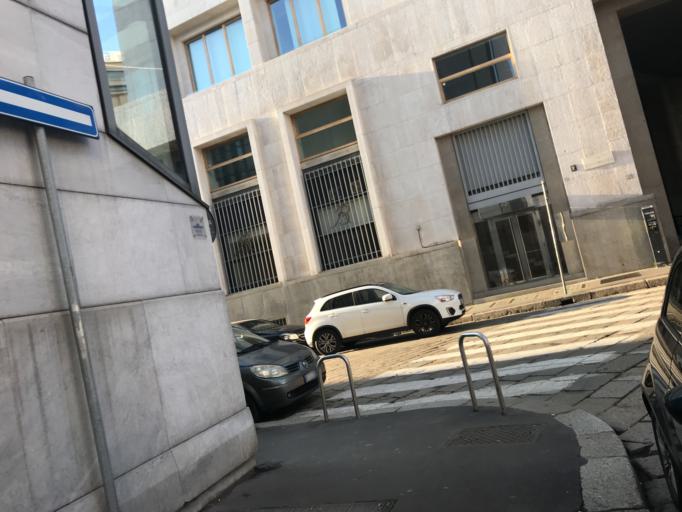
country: IT
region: Lombardy
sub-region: Citta metropolitana di Milano
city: Milano
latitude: 45.4641
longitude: 9.1846
